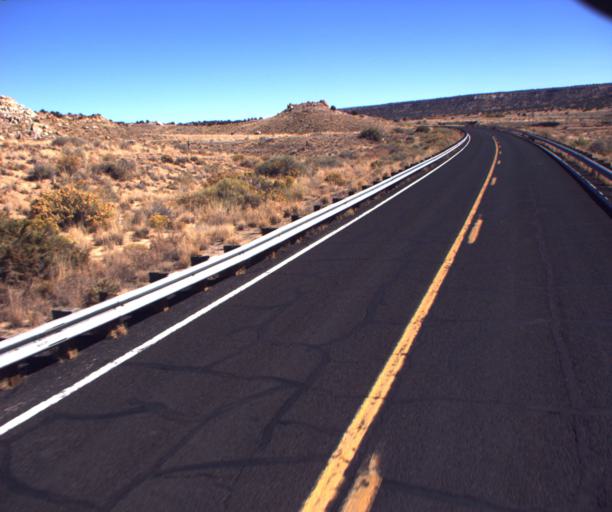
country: US
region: Arizona
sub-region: Navajo County
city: First Mesa
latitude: 35.8298
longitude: -110.2841
